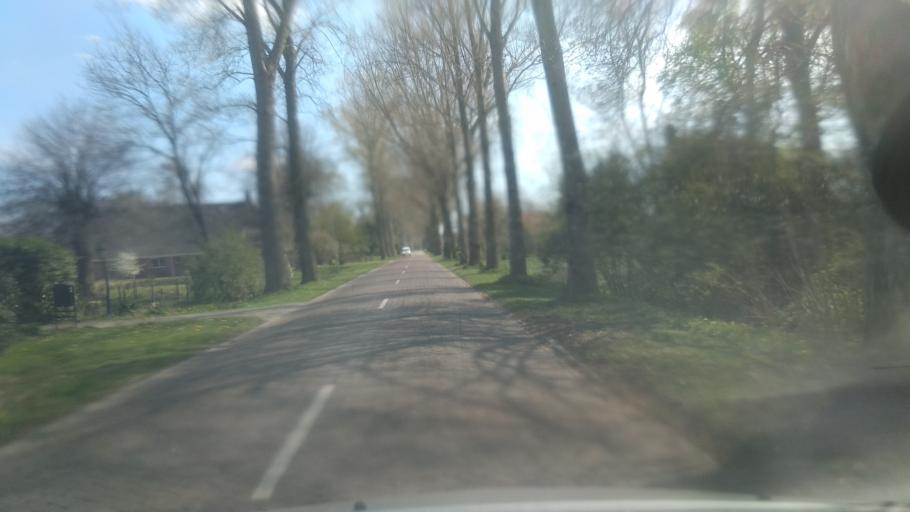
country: NL
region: Groningen
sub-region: Gemeente Stadskanaal
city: Stadskanaal
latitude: 52.9264
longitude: 6.8849
